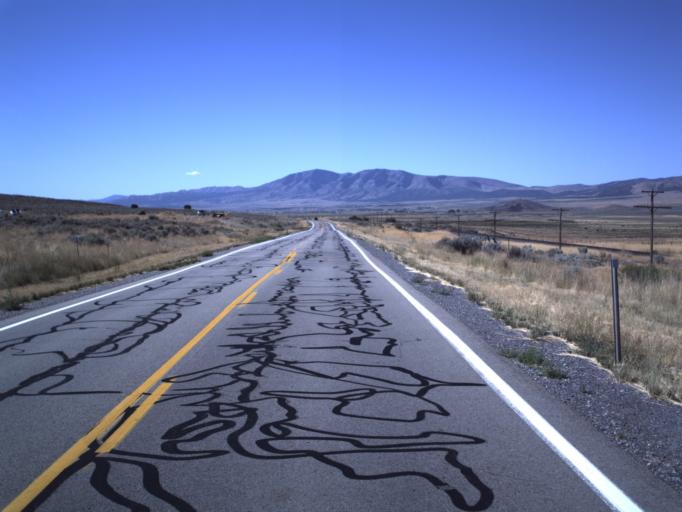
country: US
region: Utah
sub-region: Tooele County
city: Tooele
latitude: 40.4388
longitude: -112.3717
